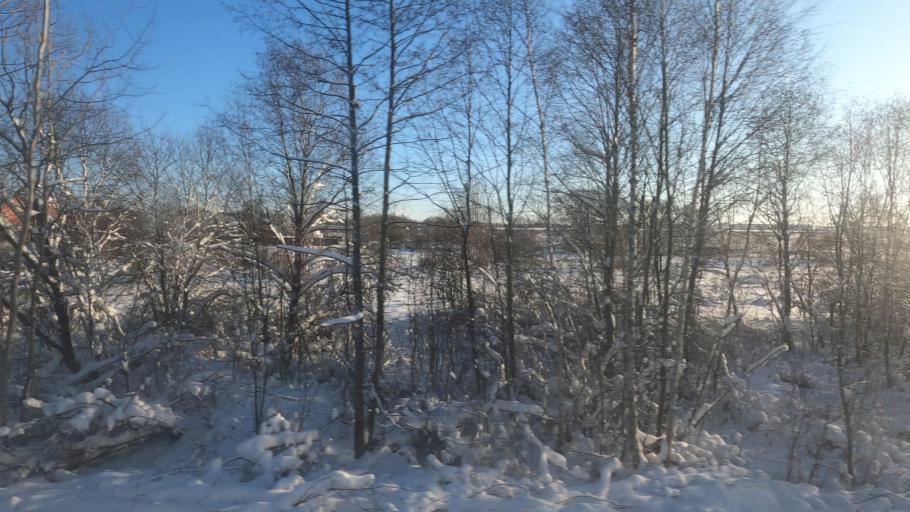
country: RU
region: Moskovskaya
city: Orud'yevo
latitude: 56.4365
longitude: 37.5063
